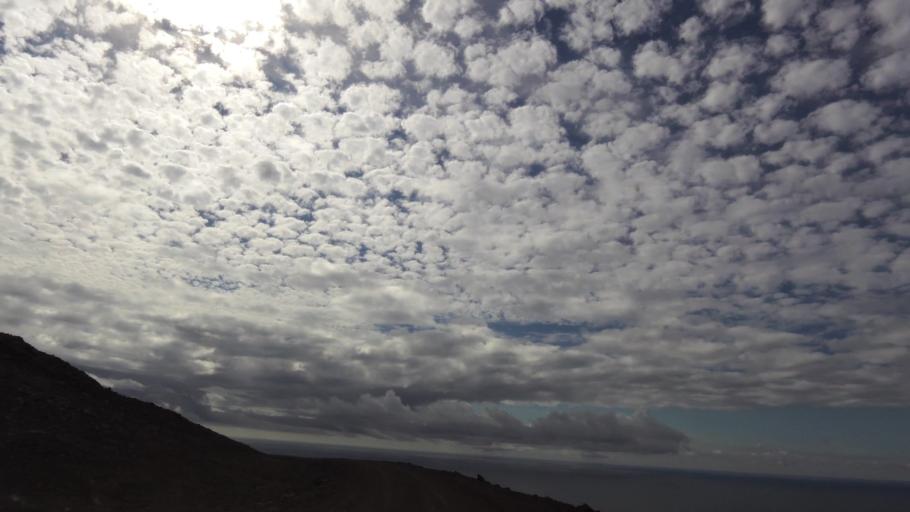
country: IS
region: West
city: Olafsvik
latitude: 65.6231
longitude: -24.2950
